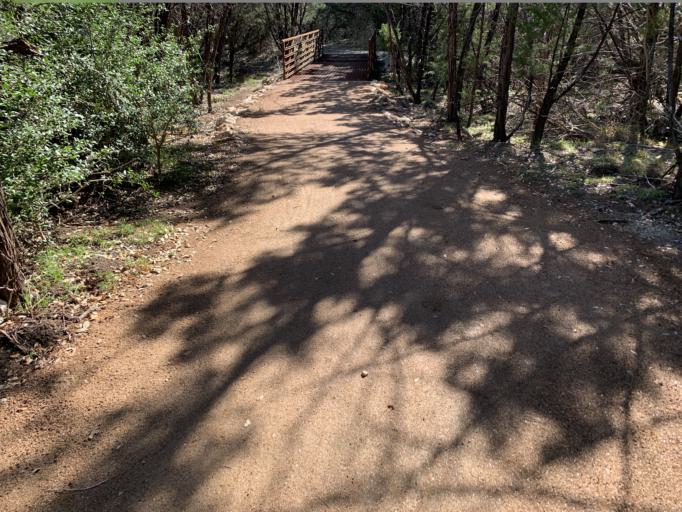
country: US
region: Texas
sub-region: Travis County
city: Shady Hollow
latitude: 30.1953
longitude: -97.8665
